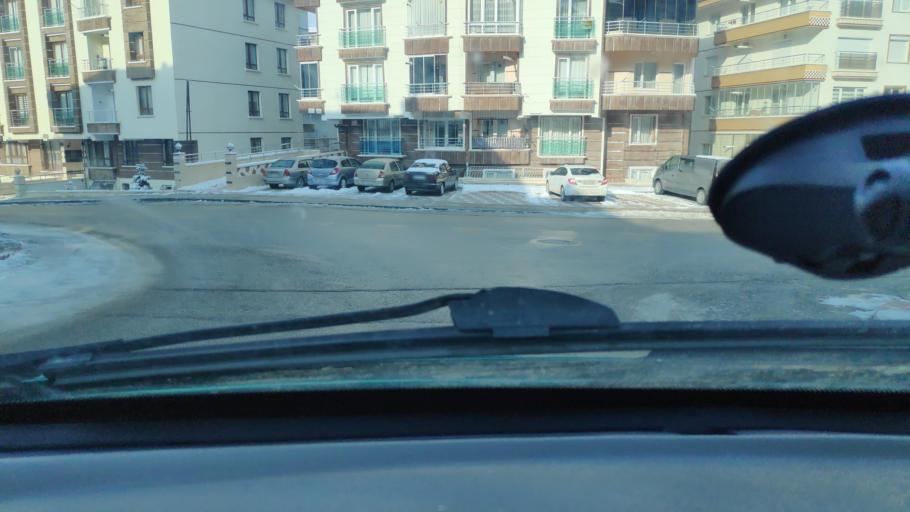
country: TR
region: Ankara
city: Ankara
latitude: 40.0130
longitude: 32.8441
